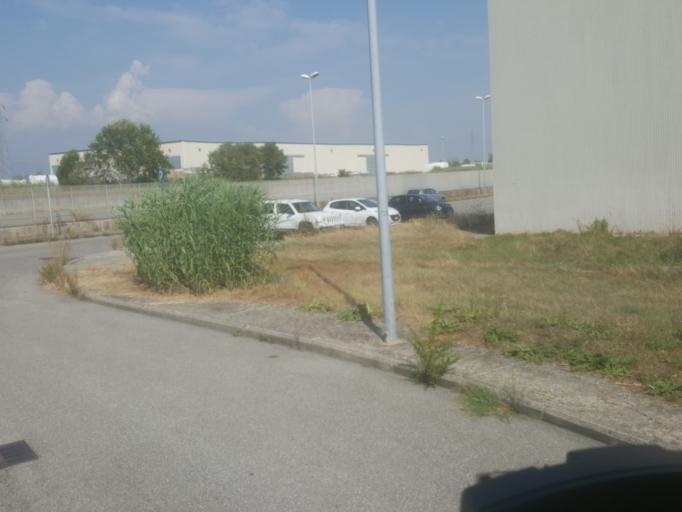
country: IT
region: Tuscany
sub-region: Provincia di Livorno
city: Guasticce
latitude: 43.5945
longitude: 10.3923
